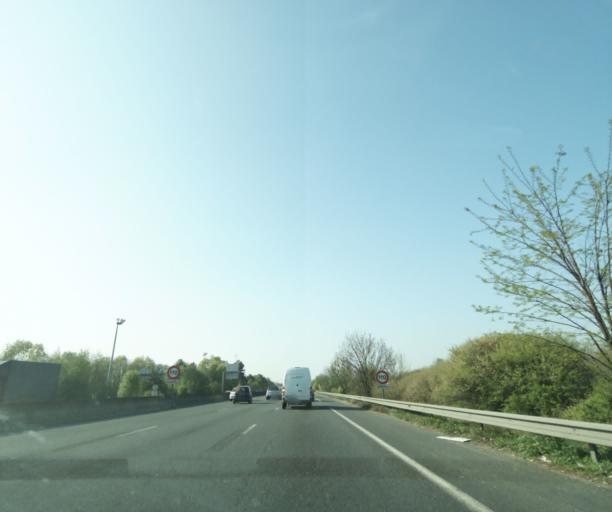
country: FR
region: Ile-de-France
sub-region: Departement de l'Essonne
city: Grigny
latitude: 48.6432
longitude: 2.3914
